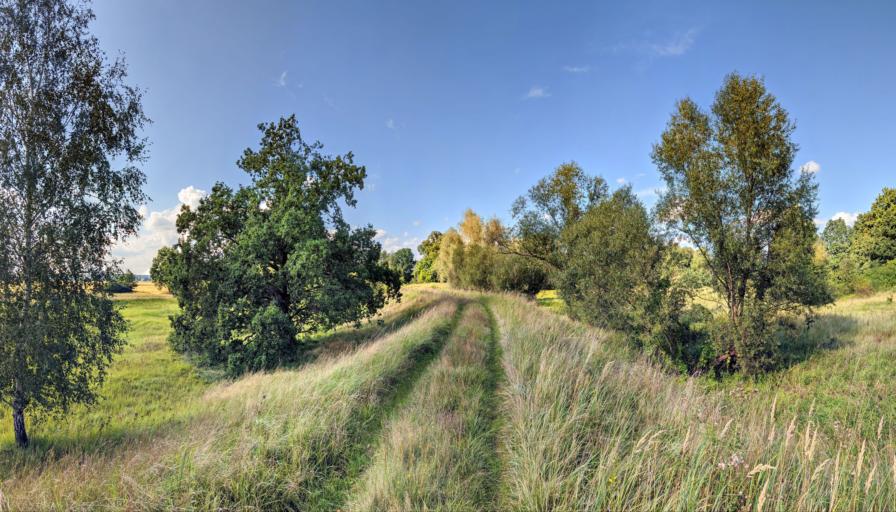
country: PL
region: Lubusz
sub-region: Powiat zielonogorski
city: Klenica
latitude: 51.9695
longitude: 15.7660
